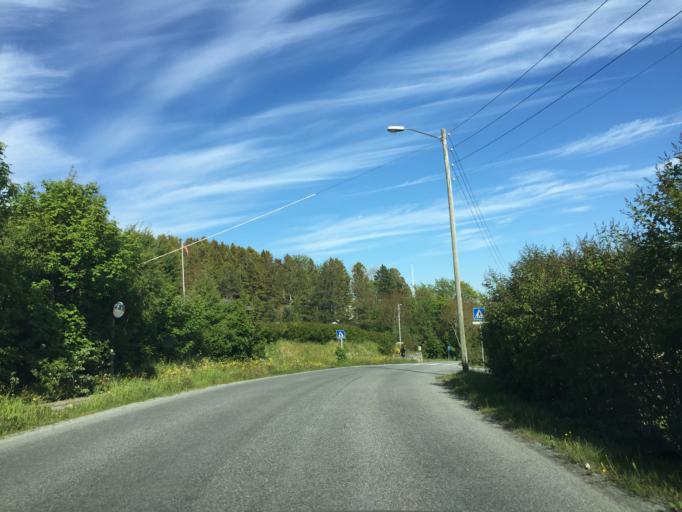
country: NO
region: Nordland
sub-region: Bodo
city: Lopsmarka
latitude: 67.2791
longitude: 14.5150
